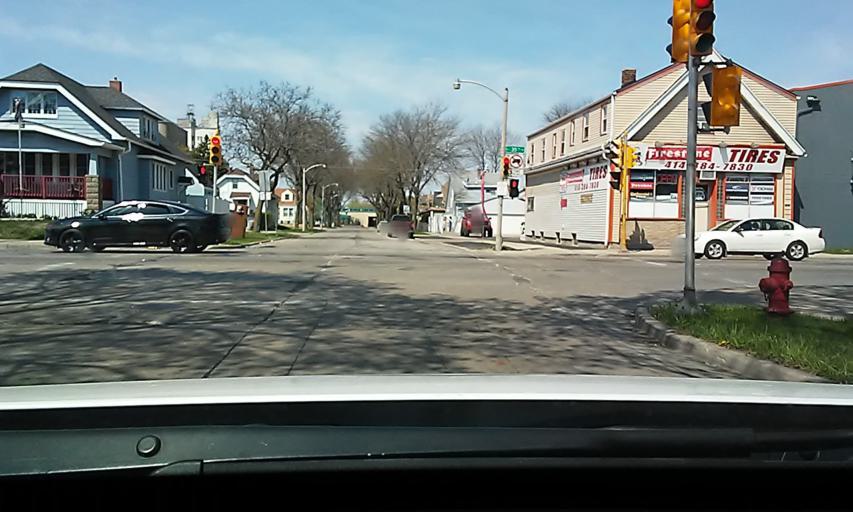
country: US
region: Wisconsin
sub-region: Milwaukee County
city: West Milwaukee
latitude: 43.0067
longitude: -87.9575
